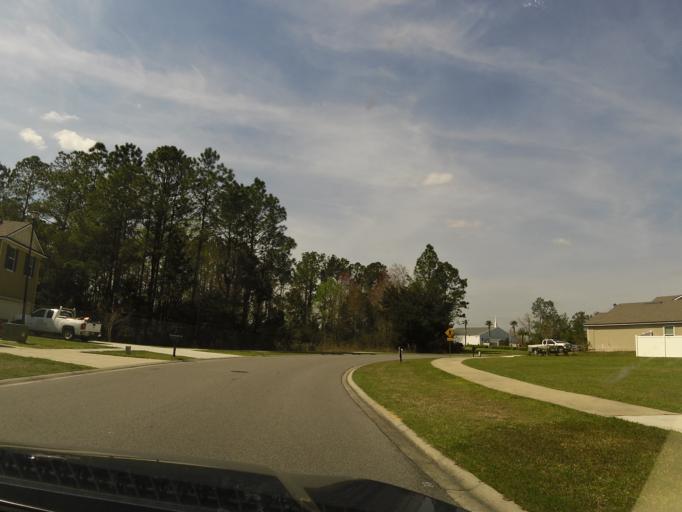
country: US
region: Florida
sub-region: Clay County
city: Middleburg
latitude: 30.0968
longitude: -81.8632
